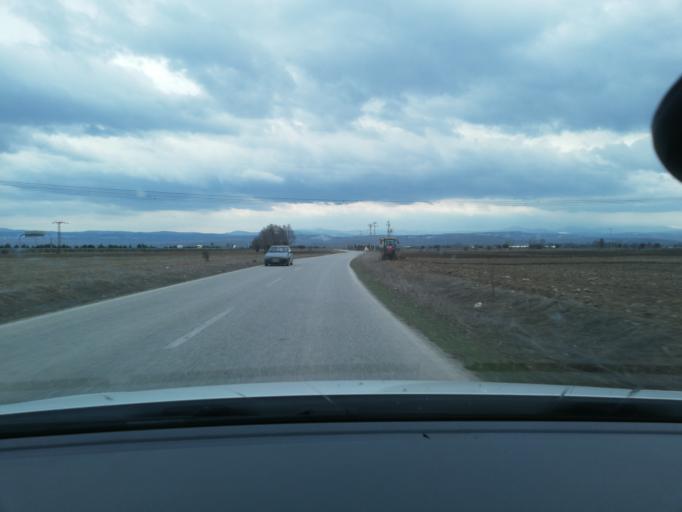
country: TR
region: Bolu
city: Gerede
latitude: 40.7766
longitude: 32.2049
